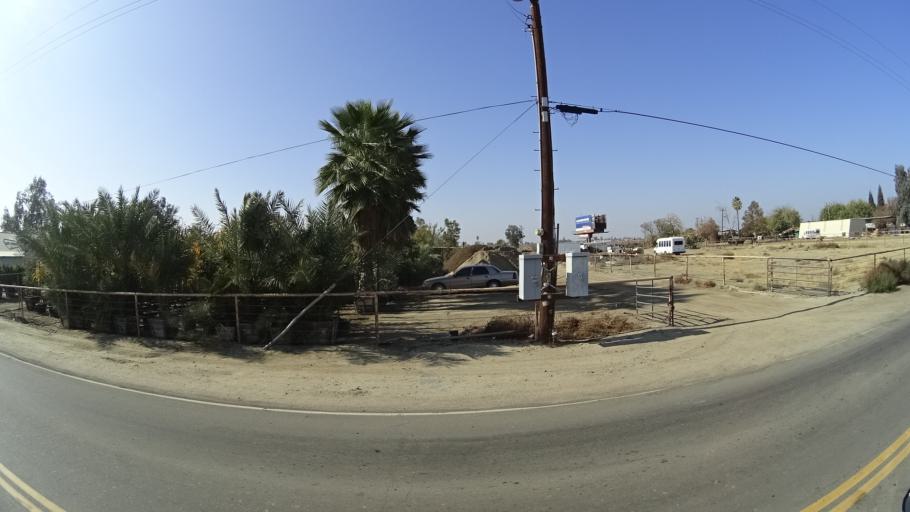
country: US
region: California
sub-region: Kern County
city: Greenfield
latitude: 35.2680
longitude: -119.0212
